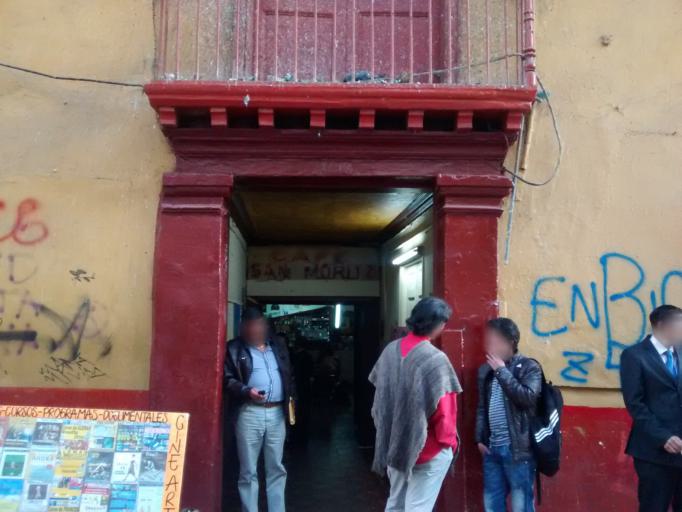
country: CO
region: Bogota D.C.
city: Bogota
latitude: 4.6030
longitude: -74.0735
